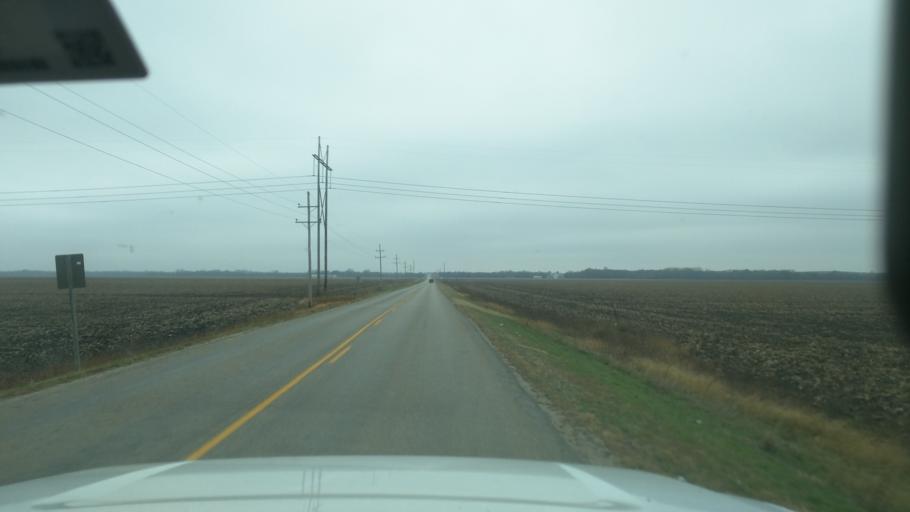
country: US
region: Kansas
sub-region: Lyon County
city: Emporia
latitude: 38.4907
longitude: -96.2528
